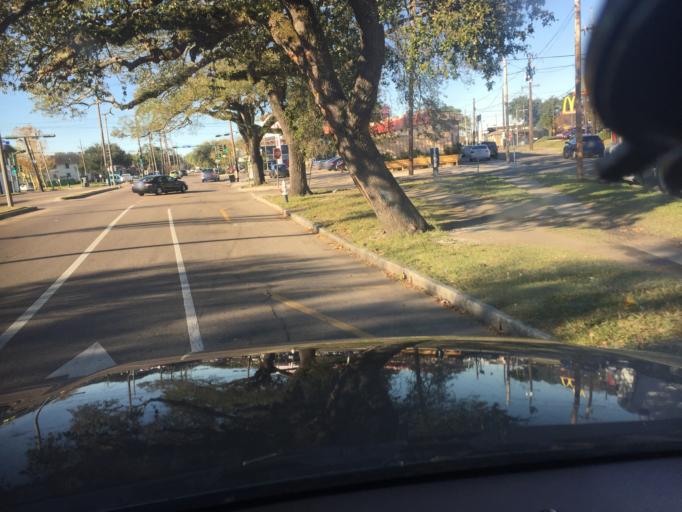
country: US
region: Louisiana
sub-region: Orleans Parish
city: New Orleans
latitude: 29.9826
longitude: -90.0712
